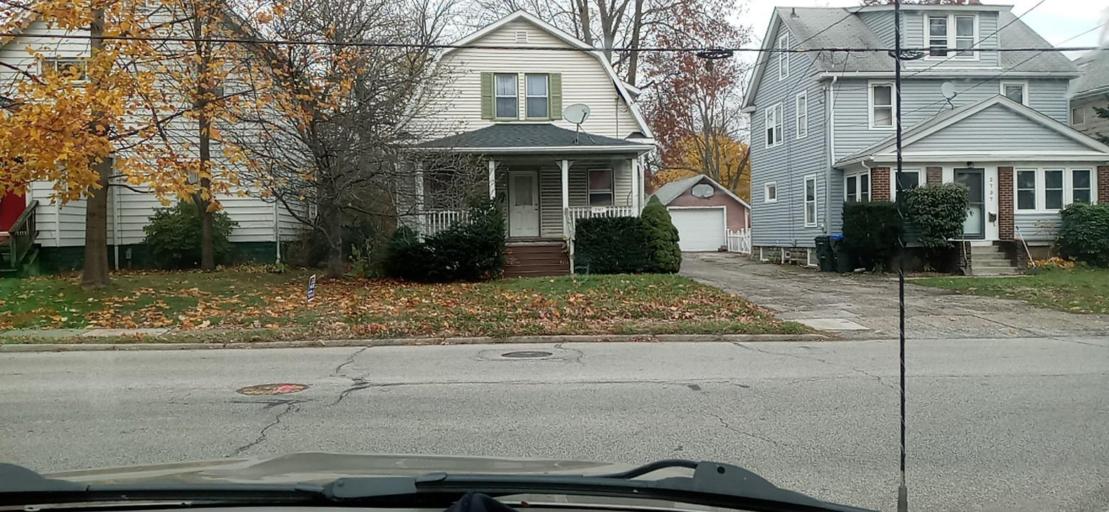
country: US
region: Ohio
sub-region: Summit County
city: Cuyahoga Falls
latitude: 41.1474
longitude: -81.4769
